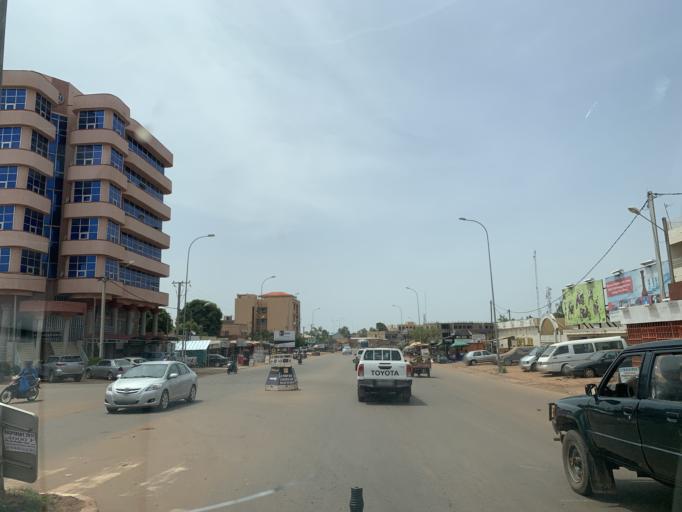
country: BF
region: Centre
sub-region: Kadiogo Province
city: Ouagadougou
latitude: 12.3381
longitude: -1.5094
